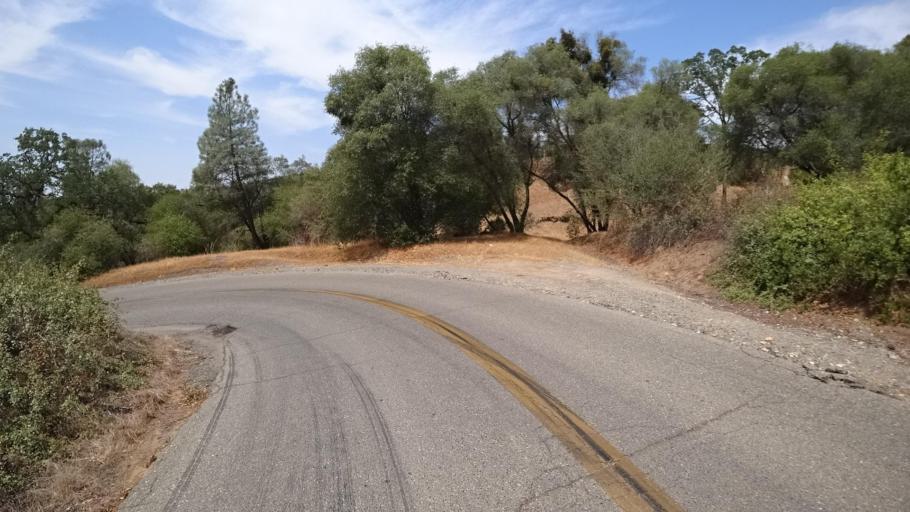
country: US
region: California
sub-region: Madera County
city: Ahwahnee
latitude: 37.4179
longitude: -119.8184
